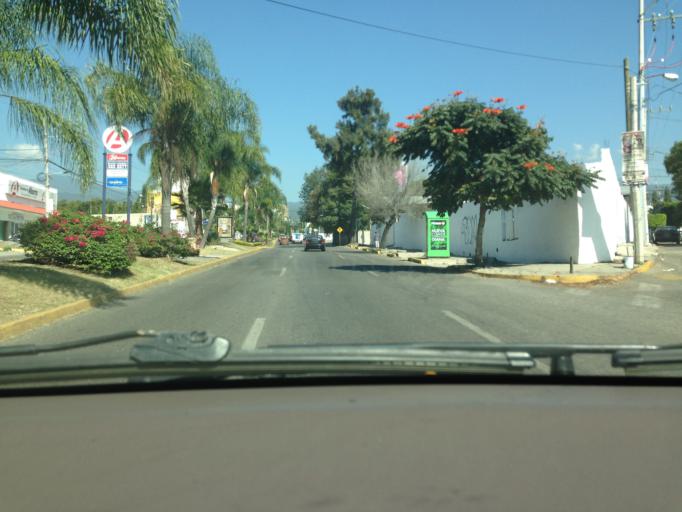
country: MX
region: Morelos
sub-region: Cuernavaca
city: Cuernavaca
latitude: 18.9484
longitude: -99.2345
